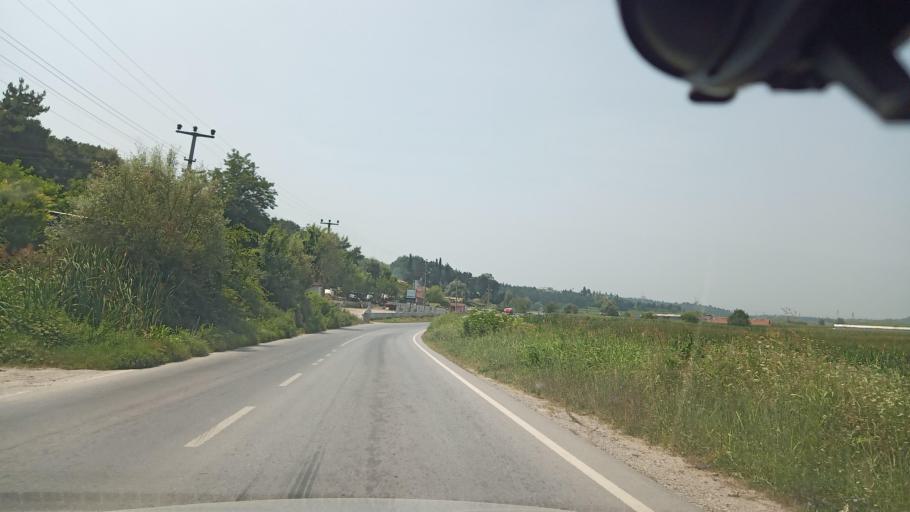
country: TR
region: Sakarya
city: Adapazari
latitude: 40.8347
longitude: 30.4073
